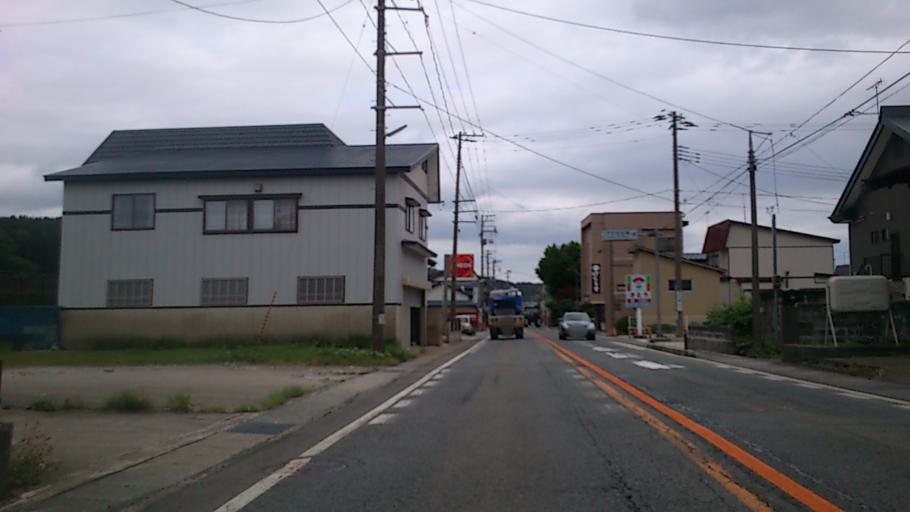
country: JP
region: Yamagata
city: Shinjo
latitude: 38.7386
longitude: 140.1432
